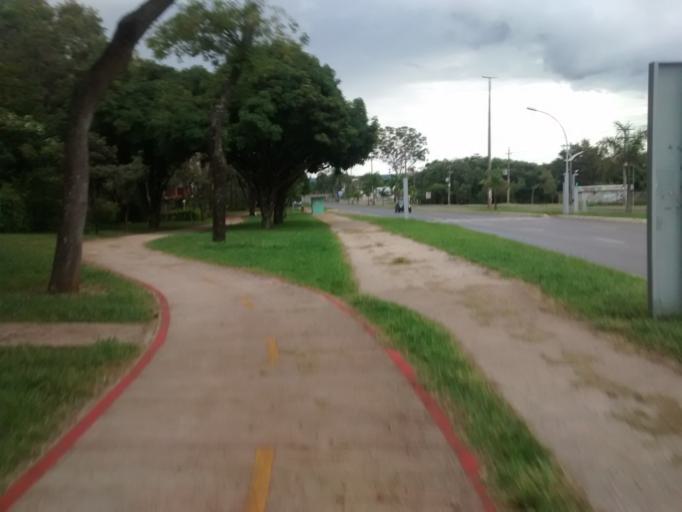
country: BR
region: Federal District
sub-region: Brasilia
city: Brasilia
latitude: -15.7650
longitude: -47.8765
